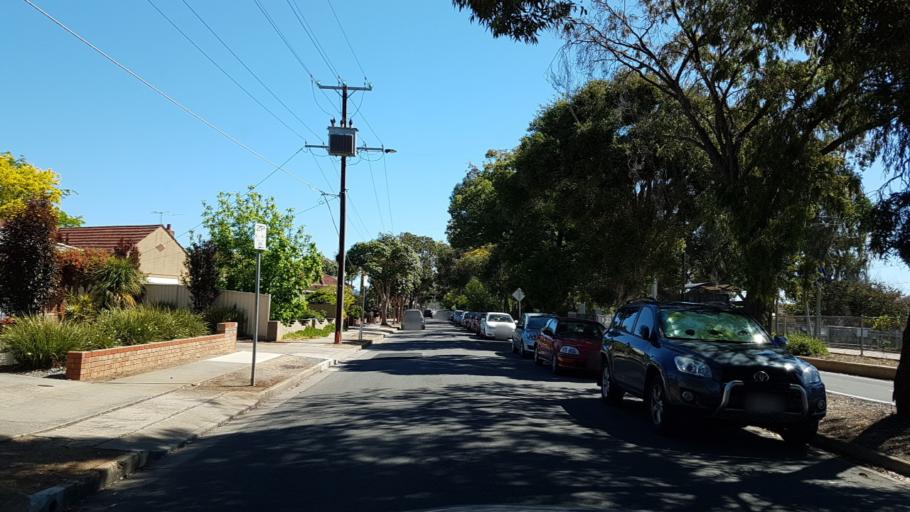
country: AU
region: South Australia
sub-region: Marion
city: South Plympton
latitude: -34.9646
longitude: 138.5604
